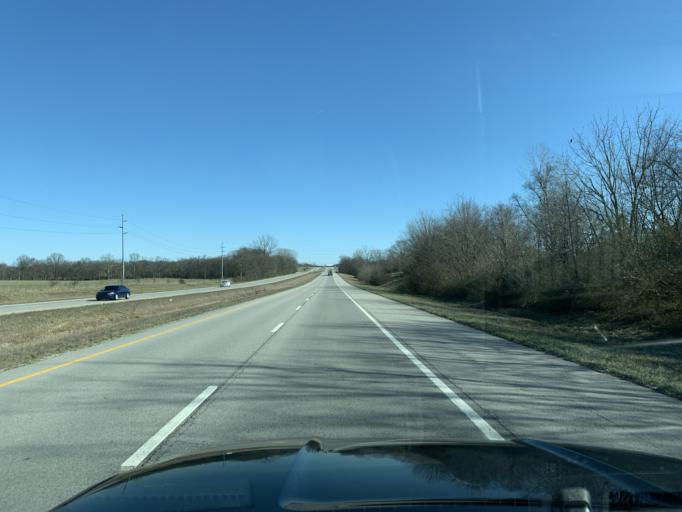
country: US
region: Tennessee
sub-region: Maury County
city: Mount Pleasant
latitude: 35.5537
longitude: -87.2026
